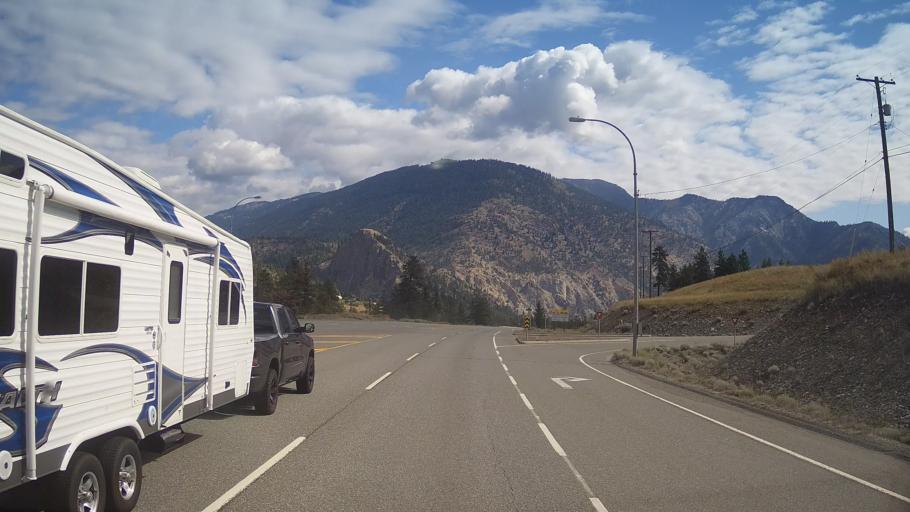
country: CA
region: British Columbia
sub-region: Thompson-Nicola Regional District
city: Ashcroft
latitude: 50.2460
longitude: -121.5696
